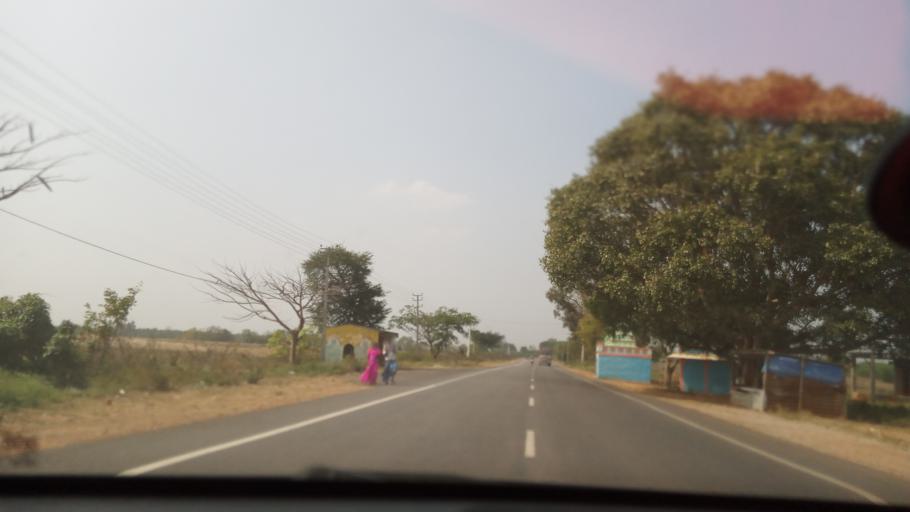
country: IN
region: Karnataka
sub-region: Mysore
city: Nanjangud
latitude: 12.0991
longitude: 76.7167
